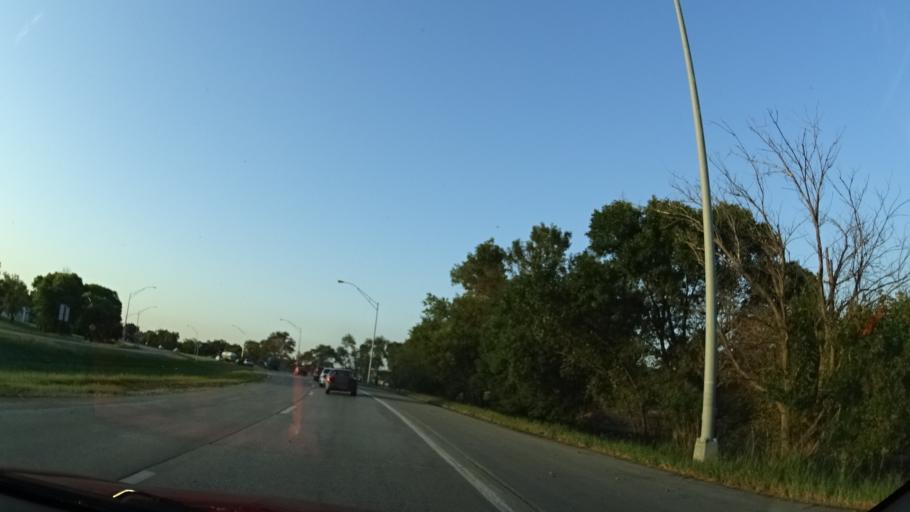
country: US
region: Iowa
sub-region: Pottawattamie County
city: Council Bluffs
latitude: 41.2400
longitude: -95.8512
